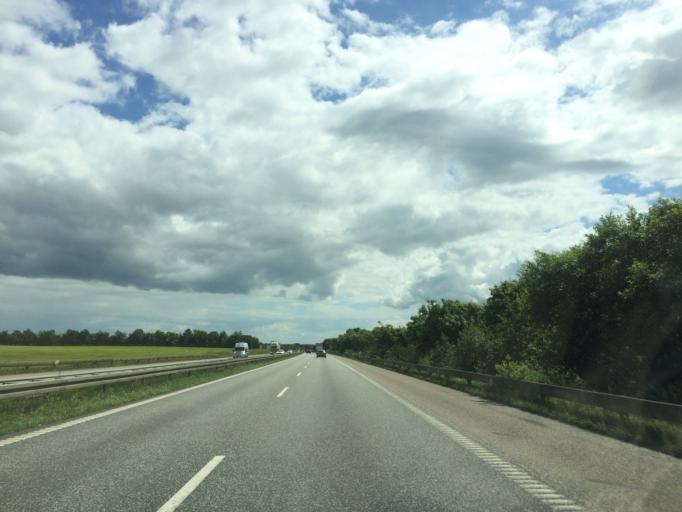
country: DK
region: North Denmark
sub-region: Mariagerfjord Kommune
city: Hobro
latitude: 56.7282
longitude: 9.7105
